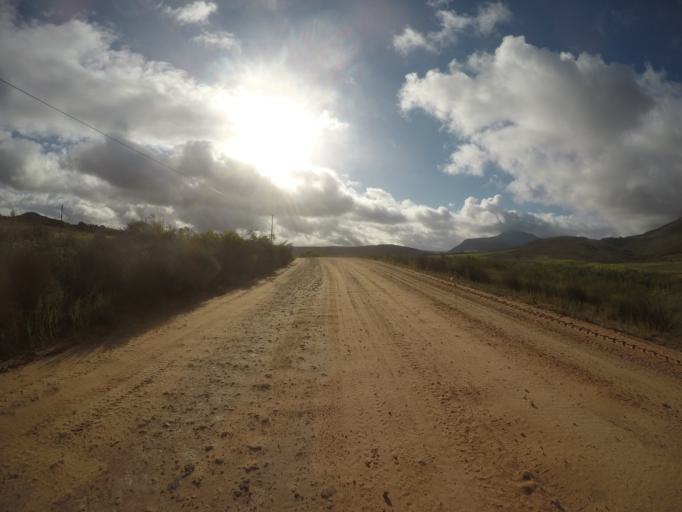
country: ZA
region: Western Cape
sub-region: West Coast District Municipality
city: Clanwilliam
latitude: -32.3430
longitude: 18.8280
